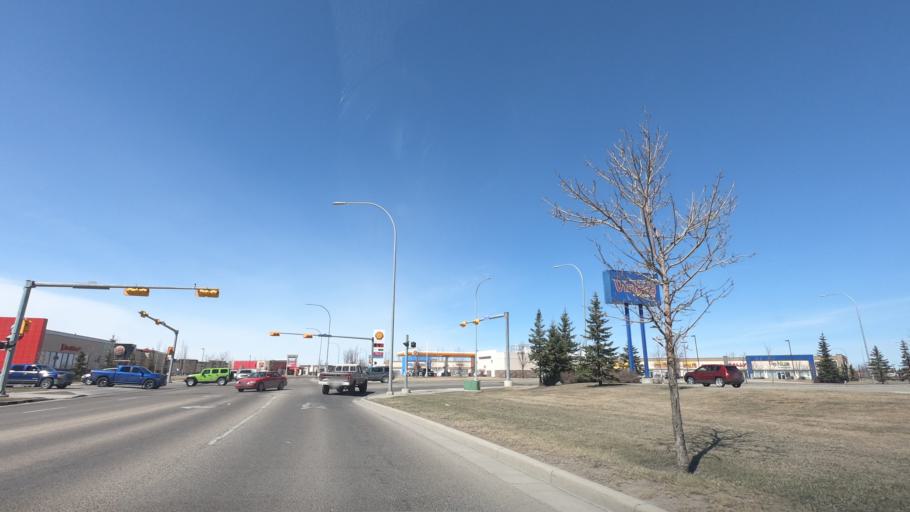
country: CA
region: Alberta
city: Airdrie
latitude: 51.2638
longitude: -114.0043
